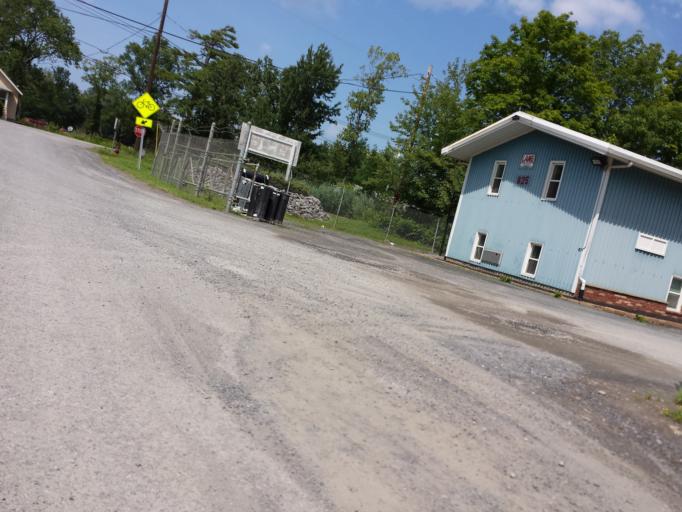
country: US
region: New York
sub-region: Saratoga County
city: Ballston Spa
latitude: 42.9714
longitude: -73.8364
